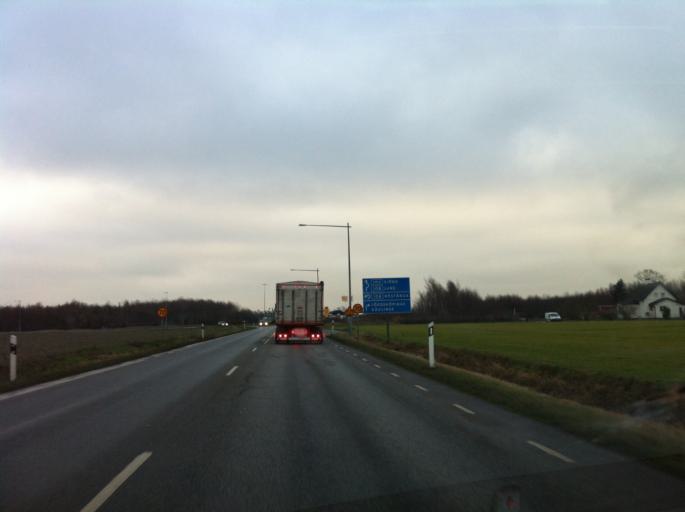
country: SE
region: Skane
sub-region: Kavlinge Kommun
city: Kaevlinge
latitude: 55.8009
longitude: 13.0922
